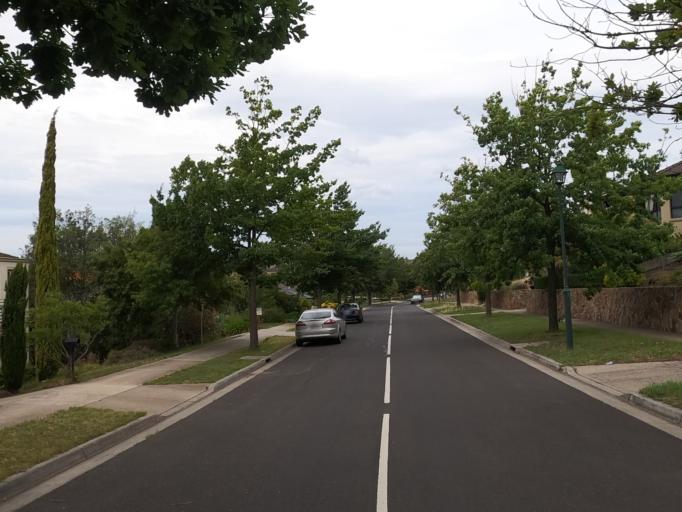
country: AU
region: Victoria
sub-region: Hume
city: Meadow Heights
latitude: -37.6512
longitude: 144.9068
